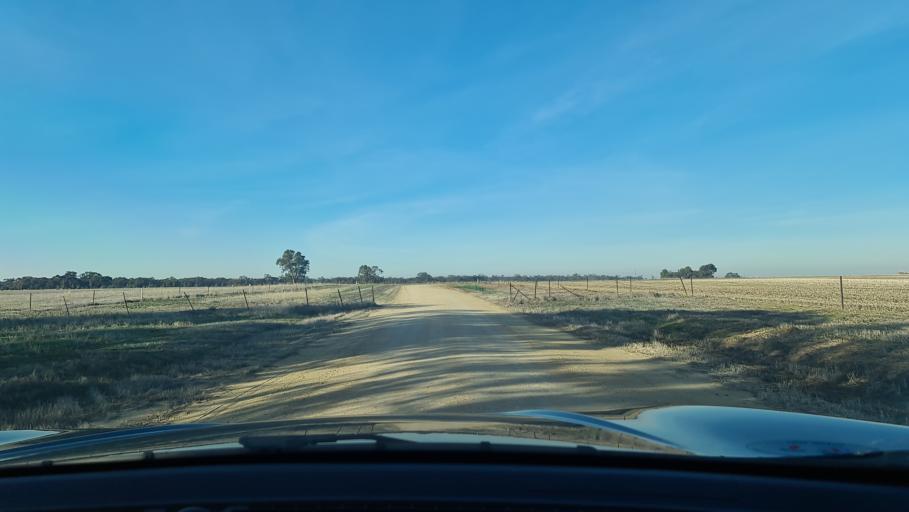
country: AU
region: Victoria
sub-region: Horsham
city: Horsham
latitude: -36.3598
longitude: 142.3963
